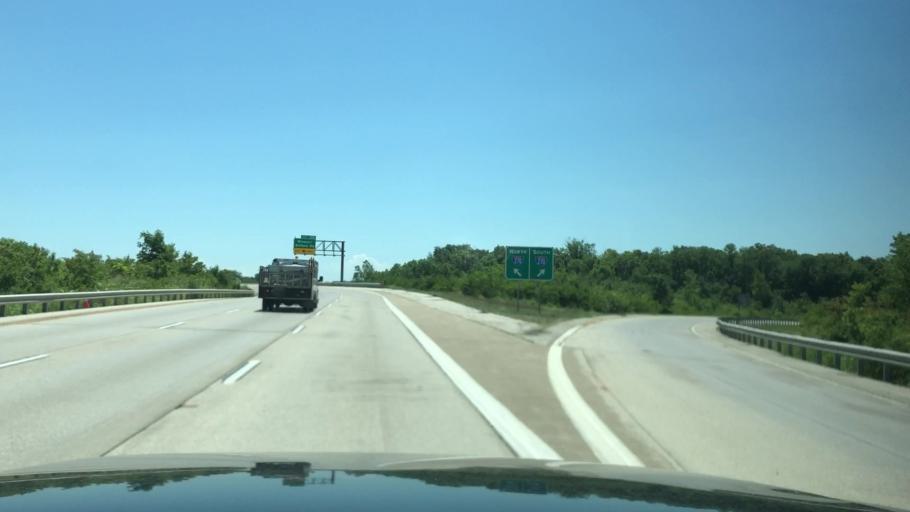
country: US
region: Missouri
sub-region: Saint Louis County
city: Bridgeton
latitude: 38.7711
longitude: -90.4085
